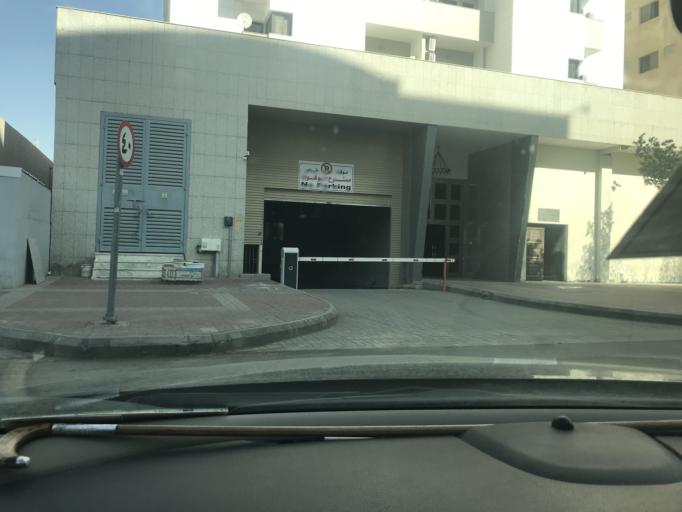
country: SA
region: Ar Riyad
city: Riyadh
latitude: 24.6878
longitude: 46.6872
